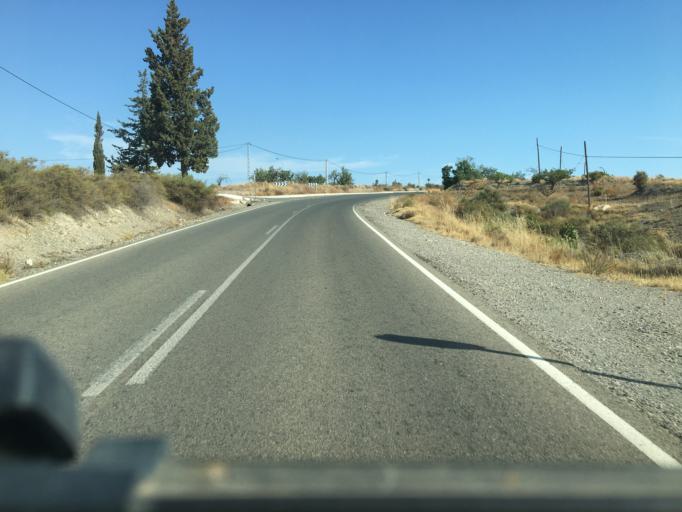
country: ES
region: Andalusia
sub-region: Provincia de Almeria
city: Huercal-Overa
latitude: 37.4529
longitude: -1.9880
